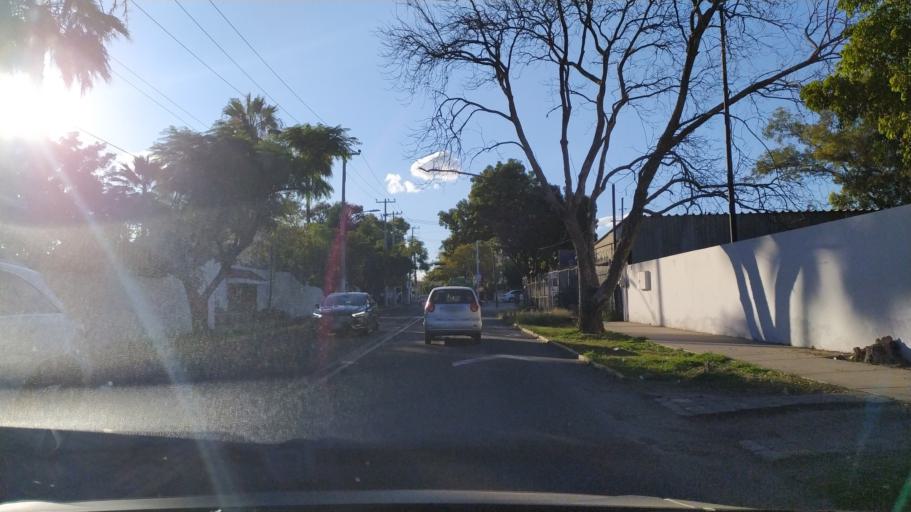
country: MX
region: Jalisco
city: Zapopan2
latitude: 20.6919
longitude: -103.4074
